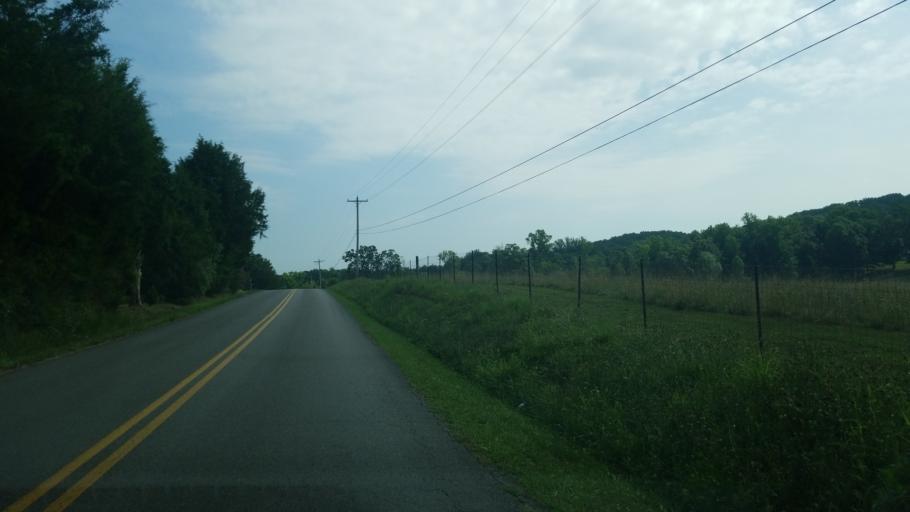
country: US
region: Tennessee
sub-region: Hamilton County
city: Apison
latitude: 35.0358
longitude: -84.9937
